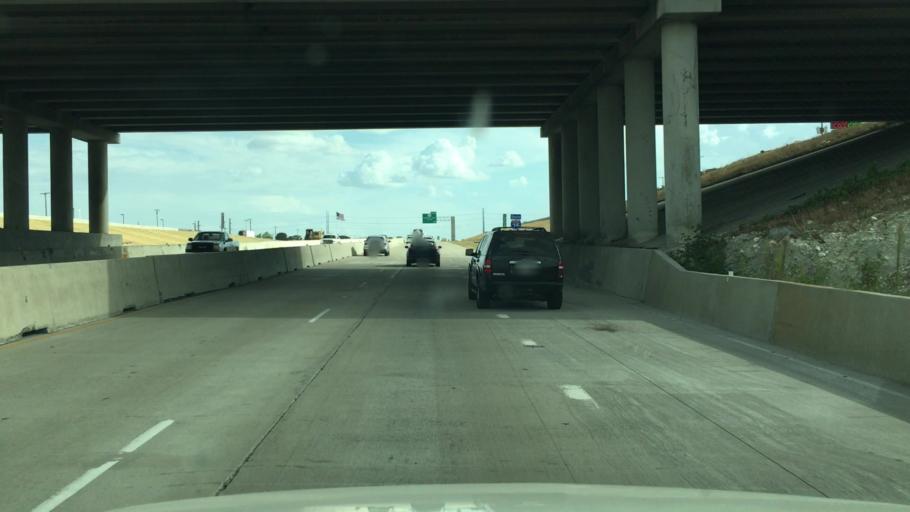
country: US
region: Texas
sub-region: Bell County
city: Temple
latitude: 31.1393
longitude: -97.3300
